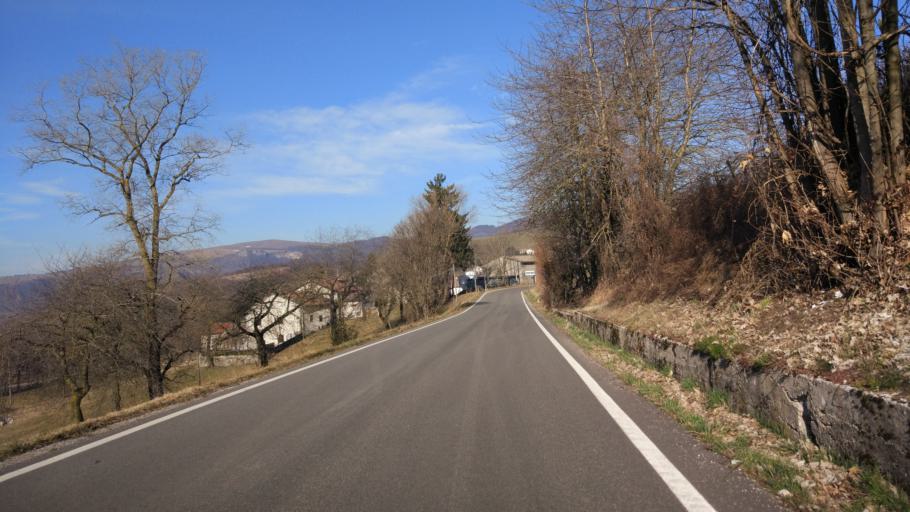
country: IT
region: Veneto
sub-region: Provincia di Verona
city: Selva di Progno
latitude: 45.6279
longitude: 11.1621
